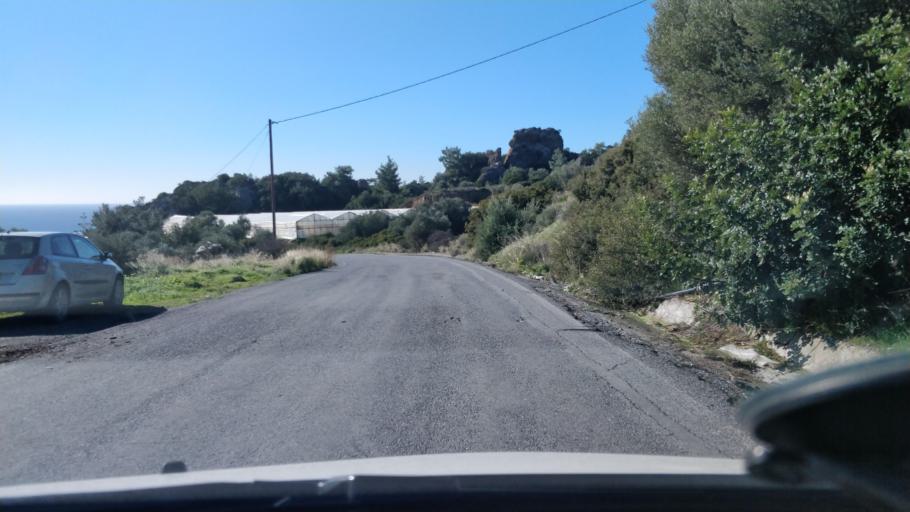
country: GR
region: Crete
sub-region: Nomos Lasithiou
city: Gra Liyia
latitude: 35.0367
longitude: 25.6695
